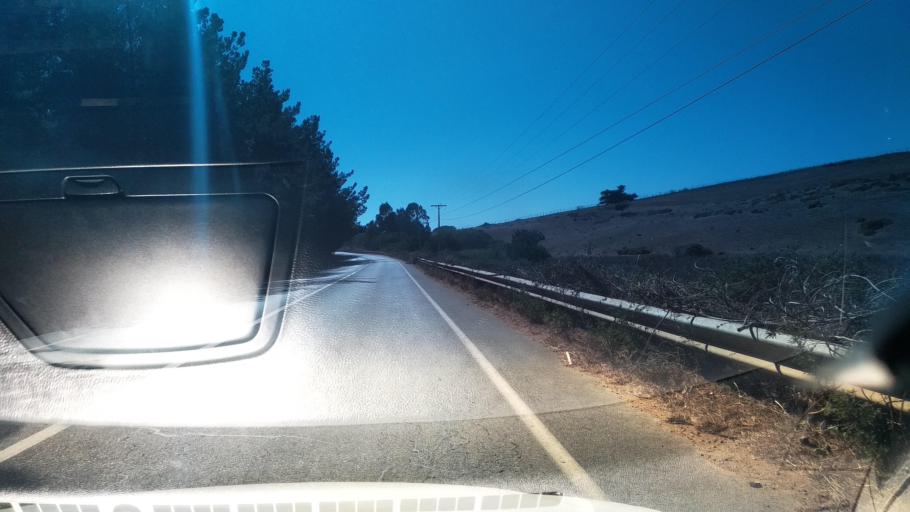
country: CL
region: O'Higgins
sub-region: Provincia de Colchagua
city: Santa Cruz
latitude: -34.4595
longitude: -72.0248
